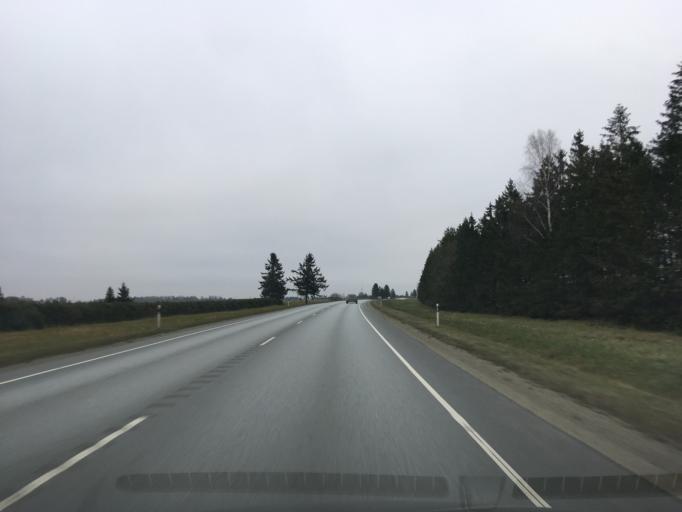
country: EE
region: Laeaene-Virumaa
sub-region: Viru-Nigula vald
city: Kunda
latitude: 59.4243
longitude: 26.6713
